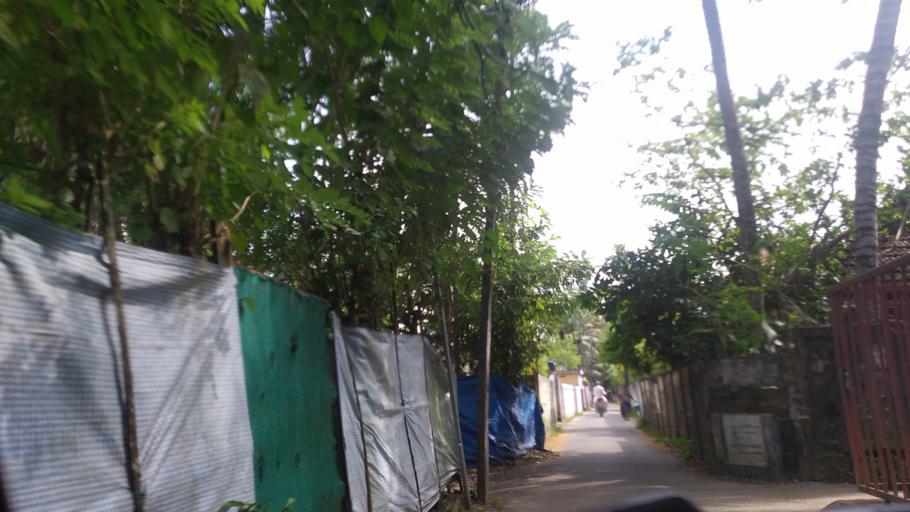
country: IN
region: Kerala
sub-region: Ernakulam
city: Elur
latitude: 10.0874
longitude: 76.2055
